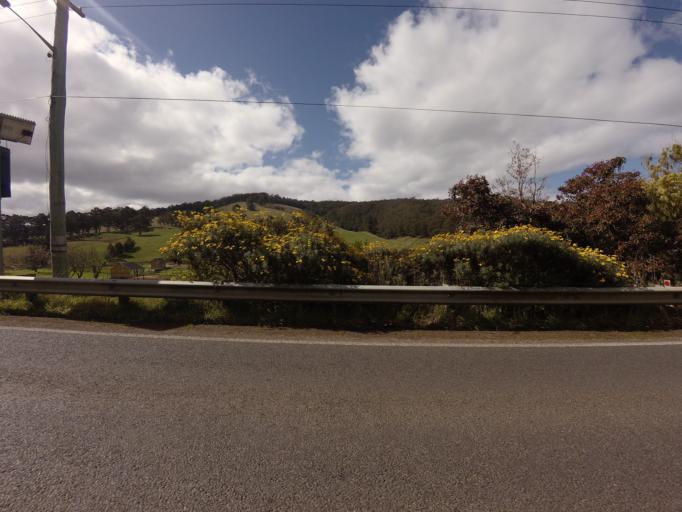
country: AU
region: Tasmania
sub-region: Huon Valley
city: Cygnet
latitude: -43.3090
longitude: 147.0123
